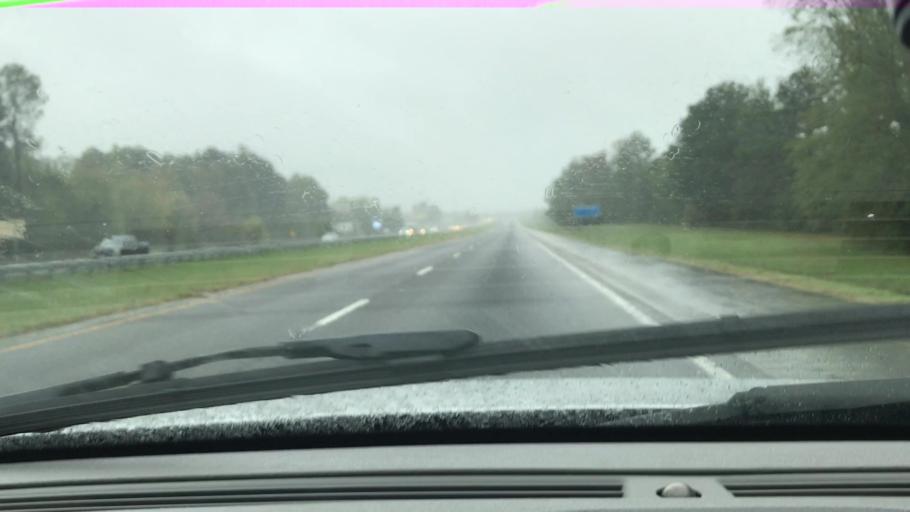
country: US
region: Alabama
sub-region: Limestone County
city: Ardmore
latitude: 34.9595
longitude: -86.8890
